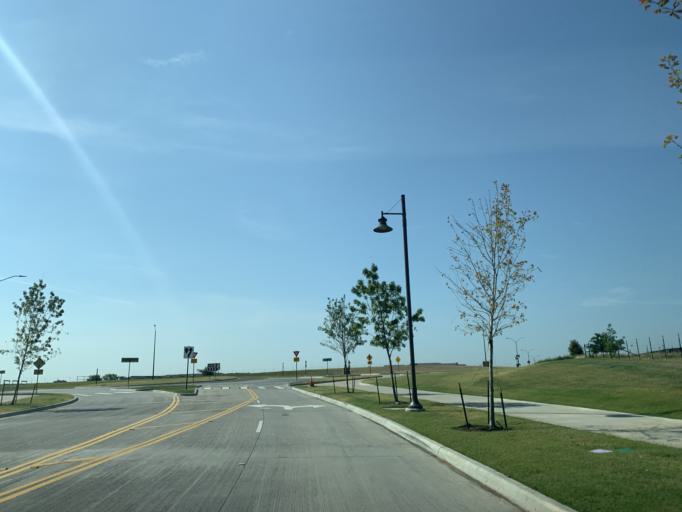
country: US
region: Texas
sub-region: Tarrant County
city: Keller
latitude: 32.9239
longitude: -97.3126
